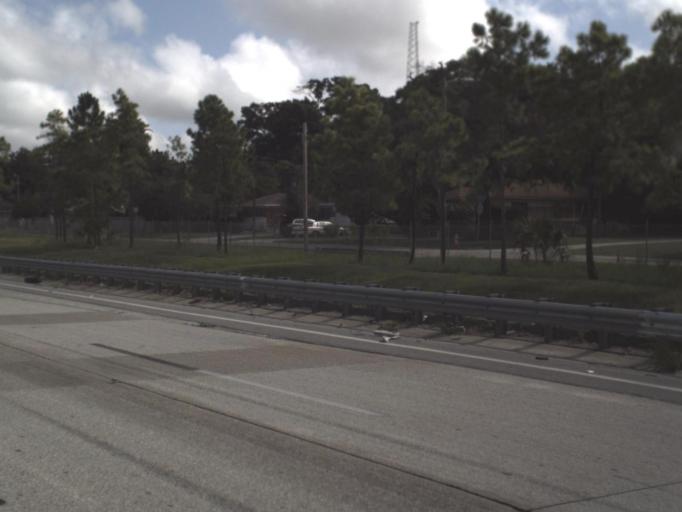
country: US
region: Florida
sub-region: Hillsborough County
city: Tampa
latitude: 27.9742
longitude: -82.4534
